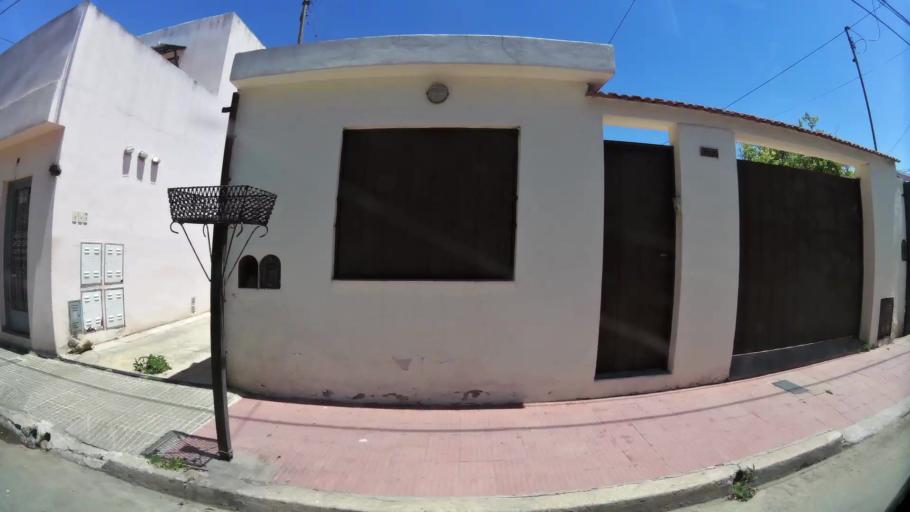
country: AR
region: Cordoba
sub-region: Departamento de Capital
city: Cordoba
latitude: -31.3877
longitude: -64.1364
